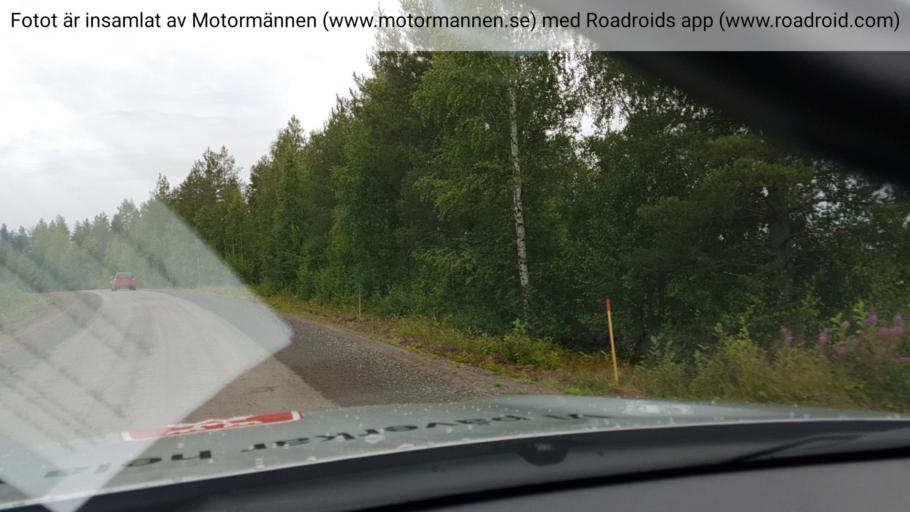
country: SE
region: Norrbotten
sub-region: Alvsbyns Kommun
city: AElvsbyn
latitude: 65.9876
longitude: 21.2075
